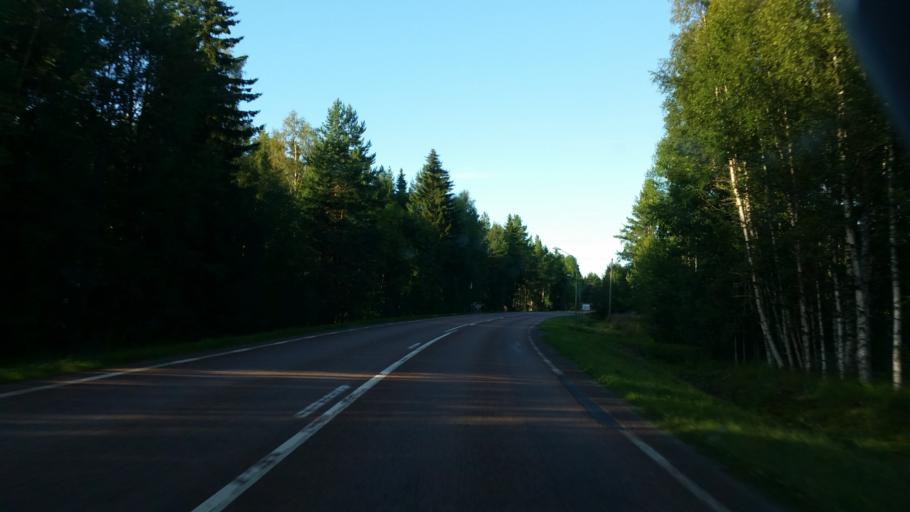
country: SE
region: Jaemtland
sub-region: Stroemsunds Kommun
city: Stroemsund
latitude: 63.9685
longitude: 15.8545
